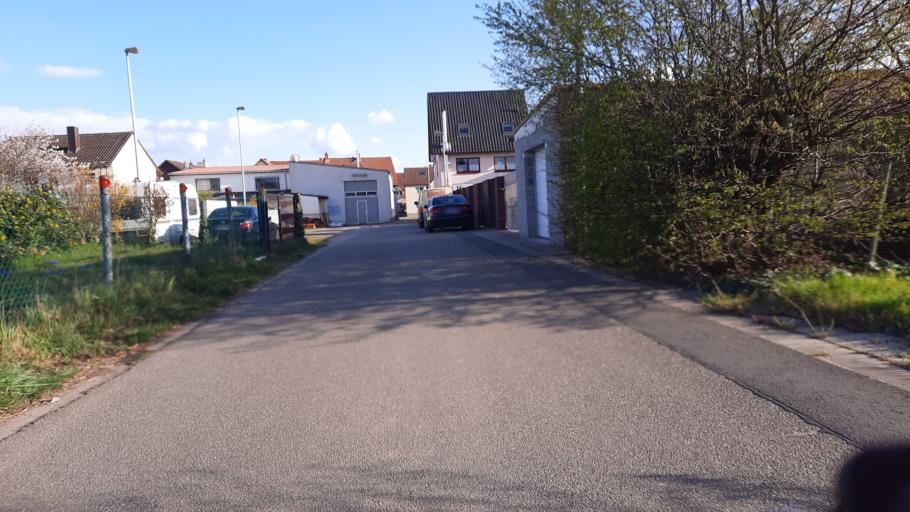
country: DE
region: Rheinland-Pfalz
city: Offstein
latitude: 49.6075
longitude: 8.2708
